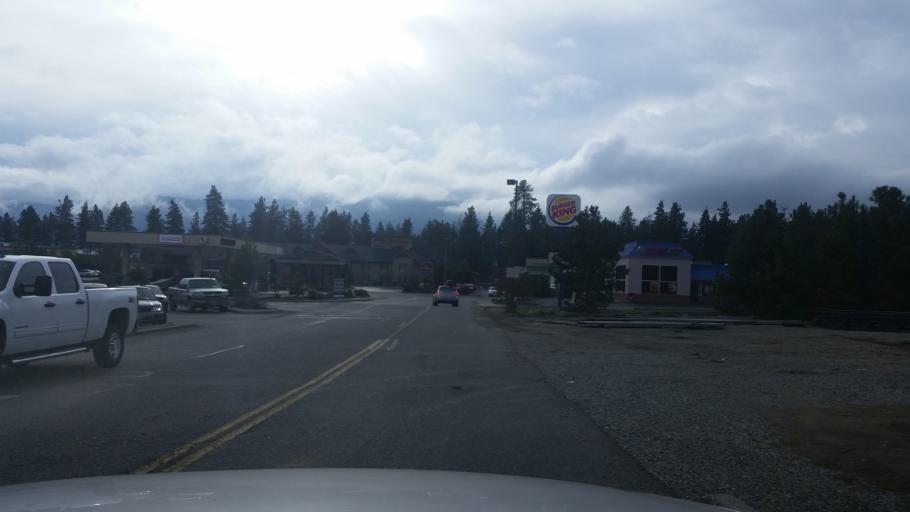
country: US
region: Washington
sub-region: Kittitas County
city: Cle Elum
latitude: 47.1960
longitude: -120.9552
